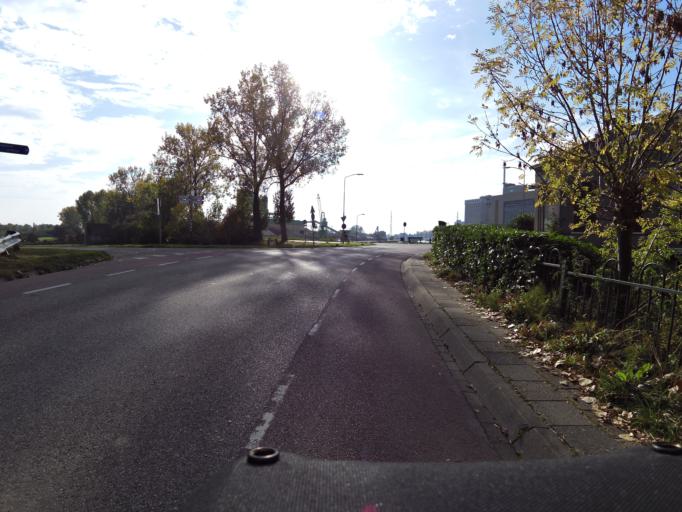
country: NL
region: Gelderland
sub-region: Gemeente Wageningen
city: Wageningen
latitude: 51.9625
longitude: 5.6592
